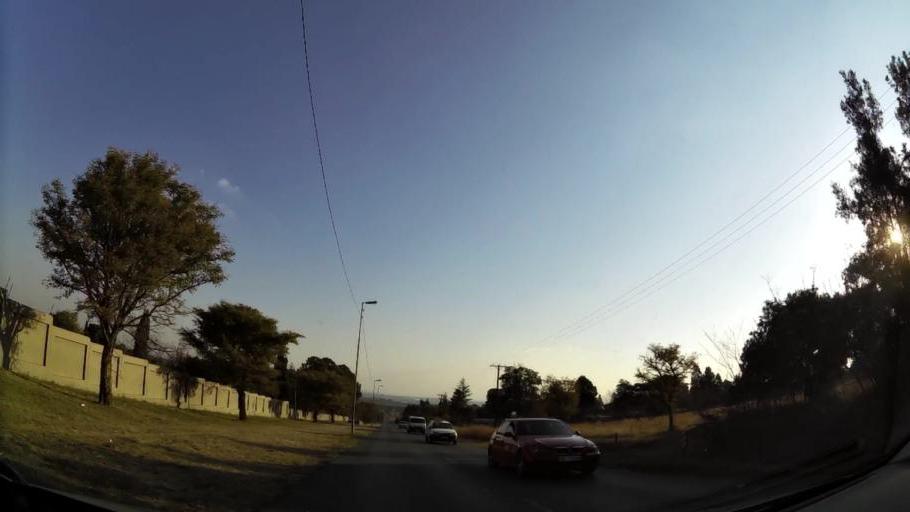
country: ZA
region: Gauteng
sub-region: City of Johannesburg Metropolitan Municipality
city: Midrand
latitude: -26.0263
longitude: 28.1480
